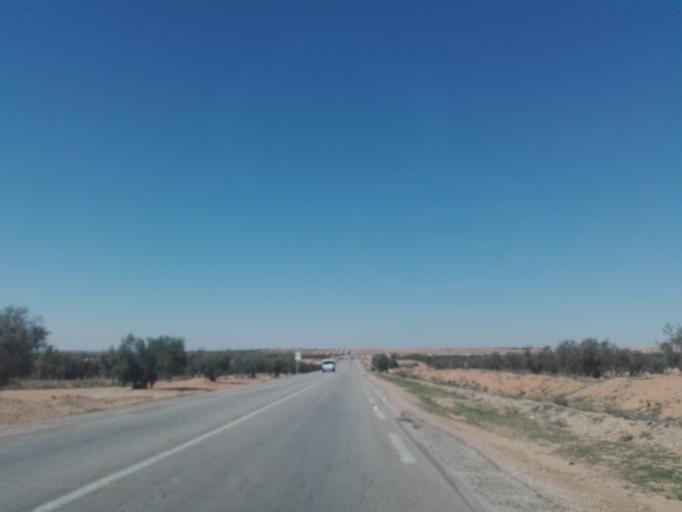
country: TN
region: Safaqis
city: Bi'r `Ali Bin Khalifah
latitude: 34.7588
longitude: 10.3002
